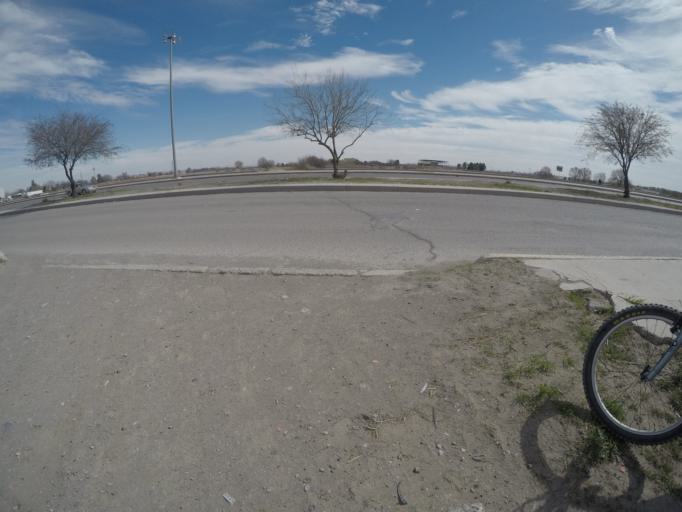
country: US
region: Texas
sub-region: El Paso County
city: Socorro
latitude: 31.6482
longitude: -106.3447
